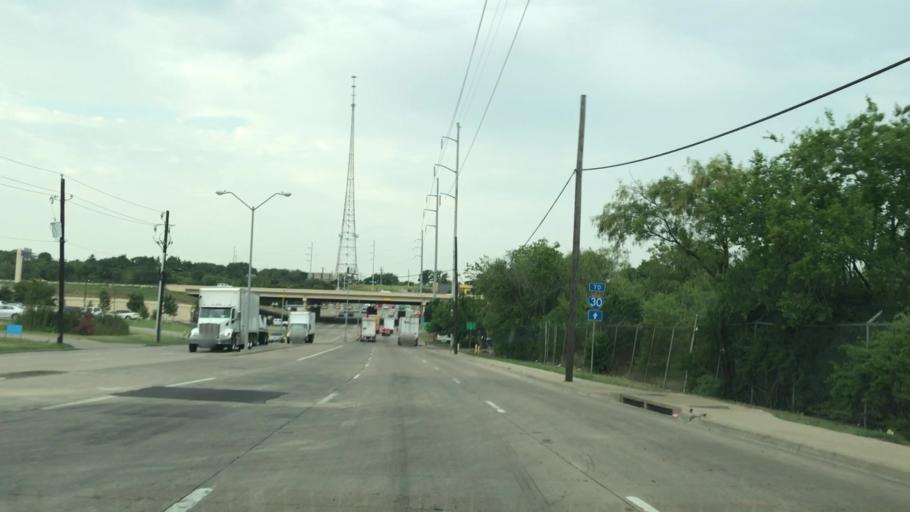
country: US
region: Texas
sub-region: Dallas County
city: Cockrell Hill
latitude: 32.7700
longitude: -96.8740
